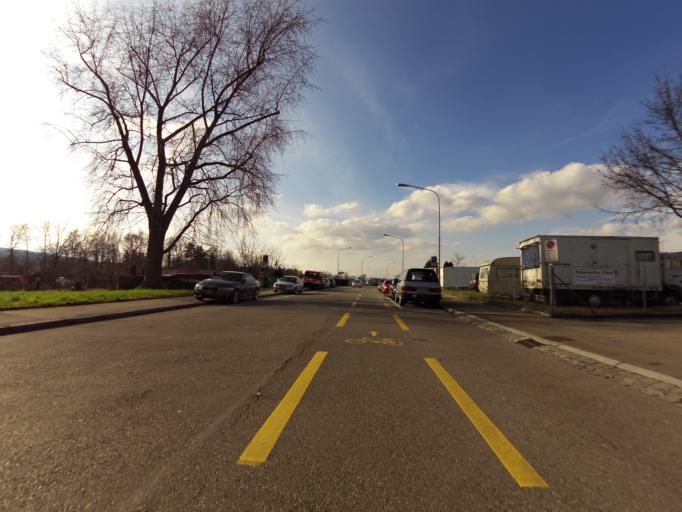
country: CH
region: Zurich
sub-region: Bezirk Zuerich
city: Zuerich (Kreis 9) / Altstetten
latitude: 47.3979
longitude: 8.4808
